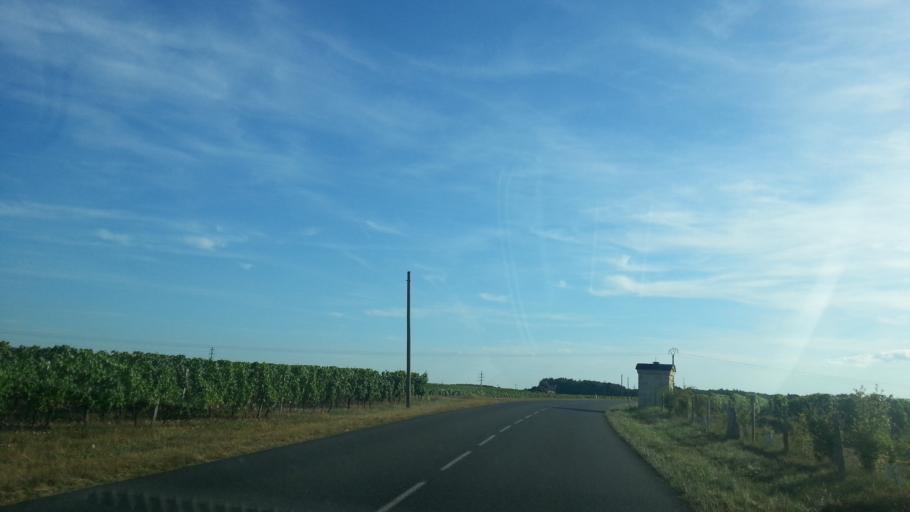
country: FR
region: Aquitaine
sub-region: Departement de la Gironde
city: Podensac
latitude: 44.6422
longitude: -0.3599
